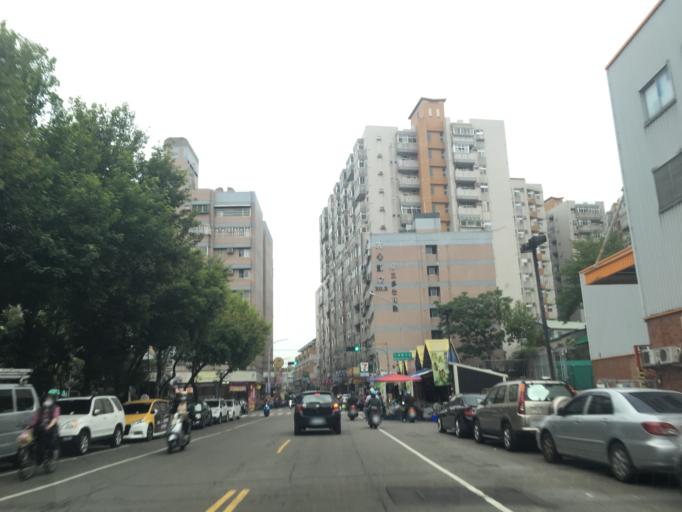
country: TW
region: Taiwan
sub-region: Taichung City
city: Taichung
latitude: 24.1737
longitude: 120.6968
